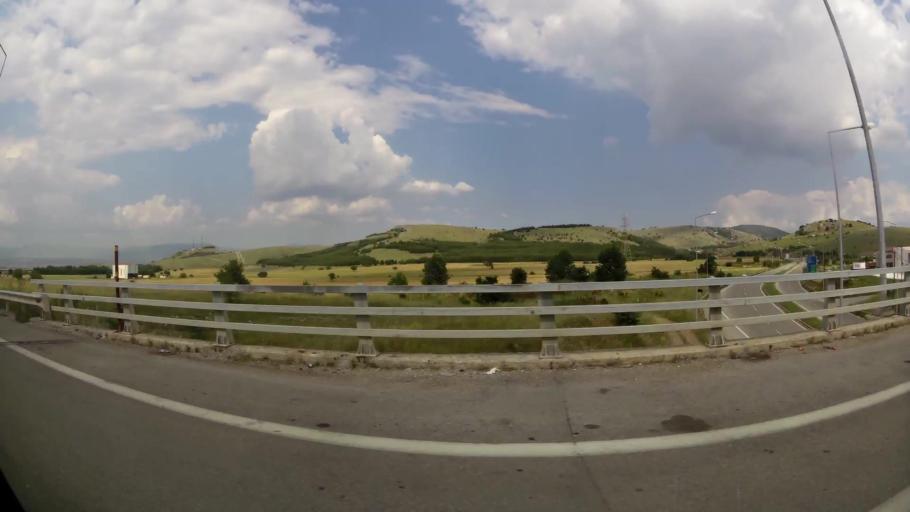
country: GR
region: West Macedonia
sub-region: Nomos Kozanis
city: Koila
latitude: 40.3441
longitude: 21.8063
